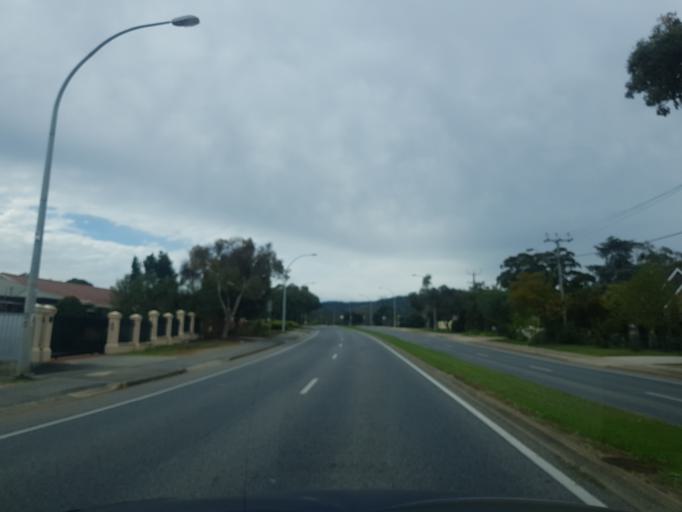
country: AU
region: South Australia
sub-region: Campbelltown
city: Athelstone
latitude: -34.8525
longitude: 138.7085
